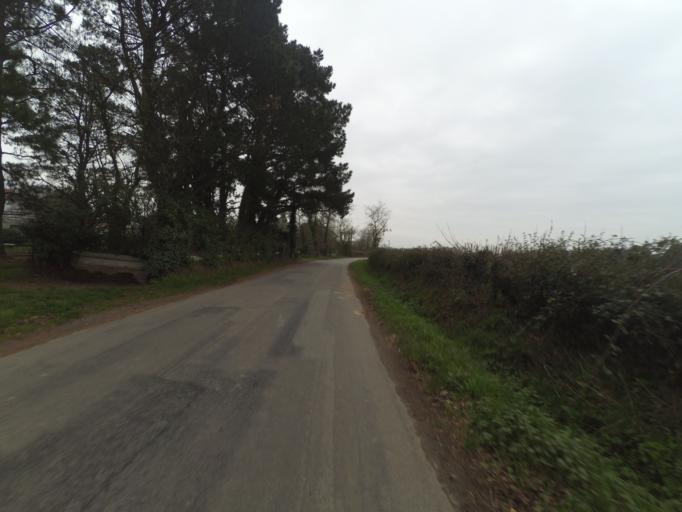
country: FR
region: Pays de la Loire
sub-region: Departement de la Loire-Atlantique
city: Sautron
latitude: 47.2531
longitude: -1.7074
